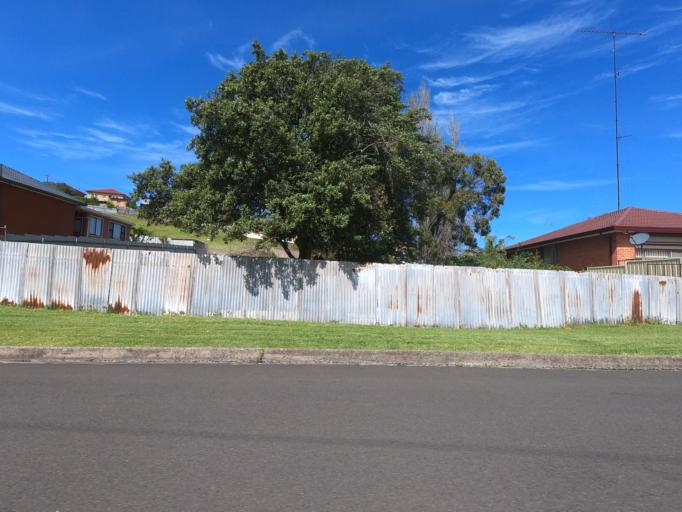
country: AU
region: New South Wales
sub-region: Wollongong
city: Lake Heights
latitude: -34.4857
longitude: 150.8743
